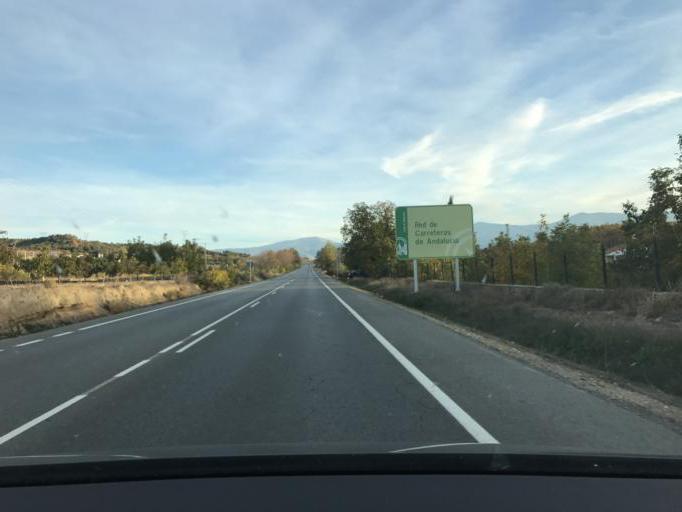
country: ES
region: Andalusia
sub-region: Provincia de Granada
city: Guadix
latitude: 37.2825
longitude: -3.1148
